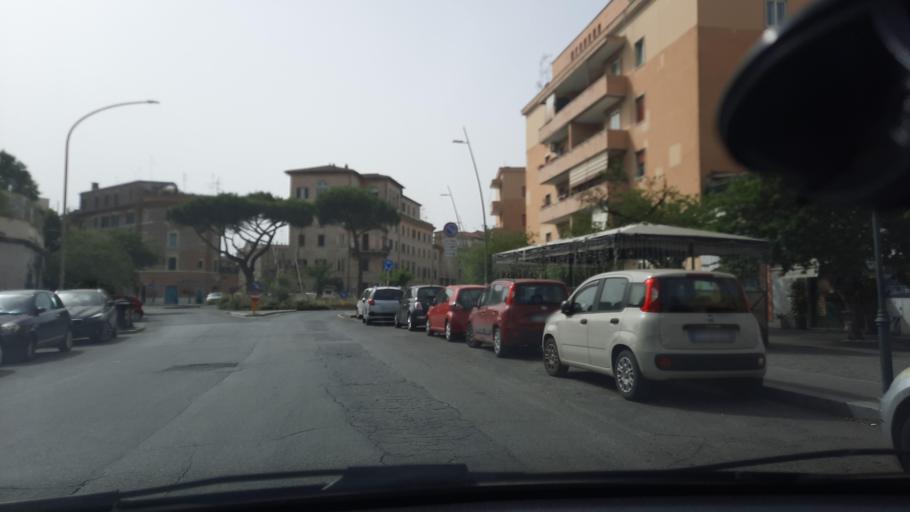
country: IT
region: Latium
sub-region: Citta metropolitana di Roma Capitale
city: Rome
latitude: 41.8607
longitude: 12.4867
